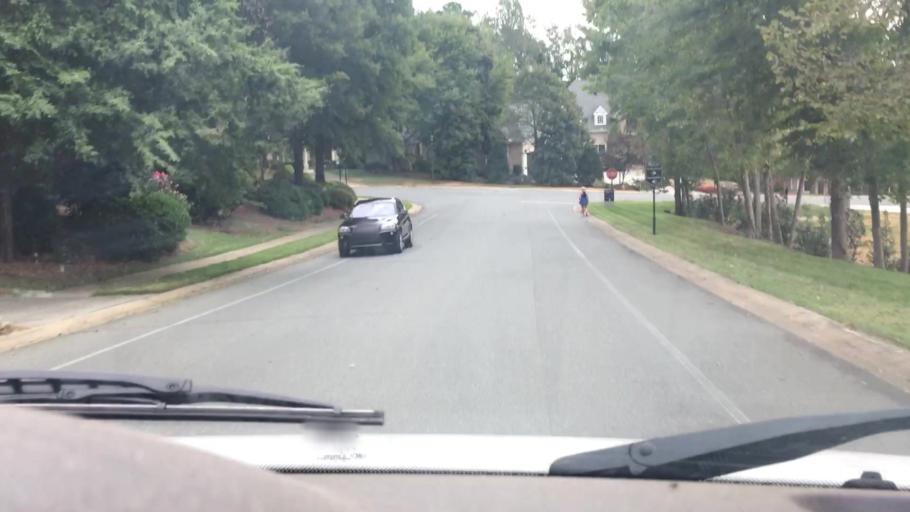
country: US
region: North Carolina
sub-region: Gaston County
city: Davidson
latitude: 35.4671
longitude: -80.8080
